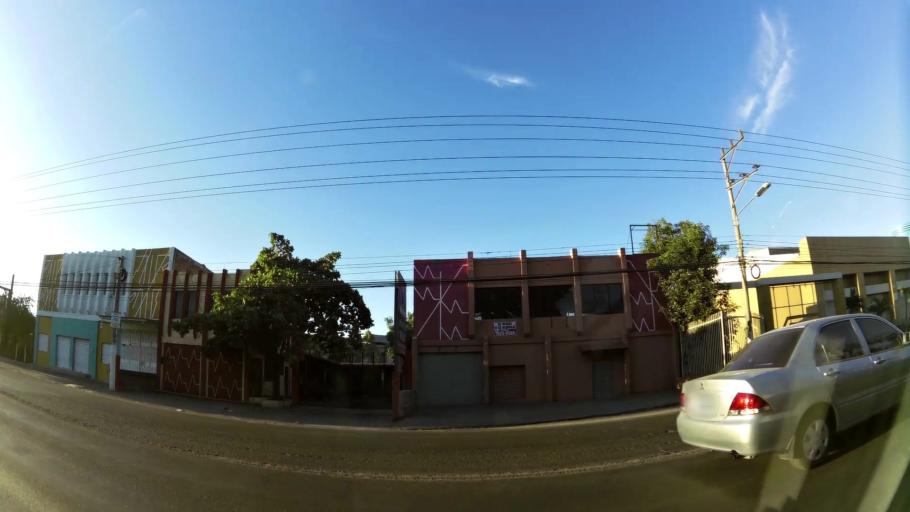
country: SV
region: San Miguel
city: San Miguel
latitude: 13.4646
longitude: -88.1698
